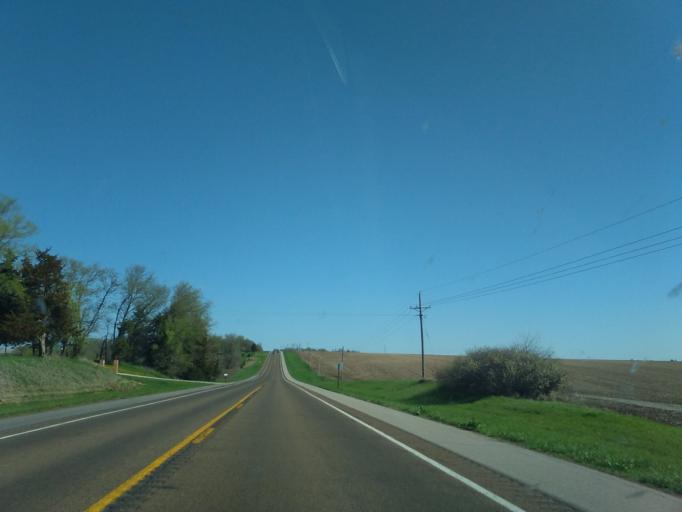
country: US
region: Nebraska
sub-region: Dodge County
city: Fremont
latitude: 41.3581
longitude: -96.5019
